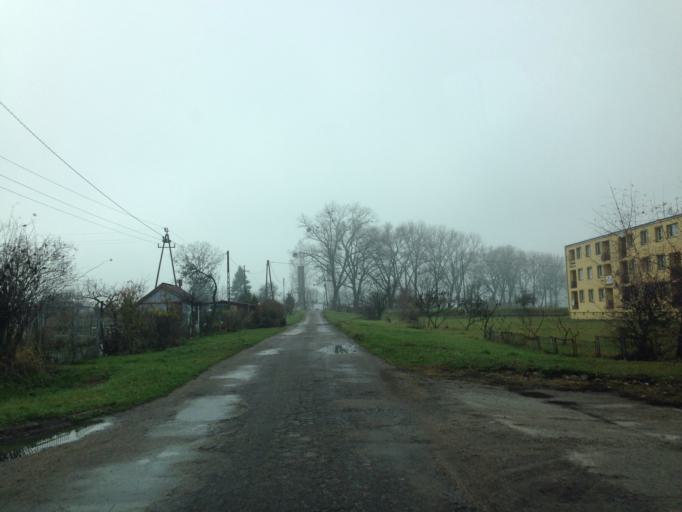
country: PL
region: Warmian-Masurian Voivodeship
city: Gierloz
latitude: 54.0077
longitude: 21.4465
